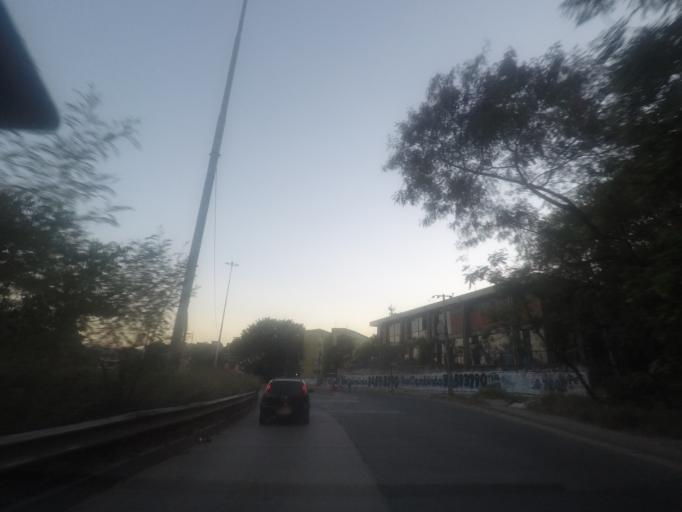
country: BR
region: Rio de Janeiro
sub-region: Duque De Caxias
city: Duque de Caxias
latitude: -22.8165
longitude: -43.2892
